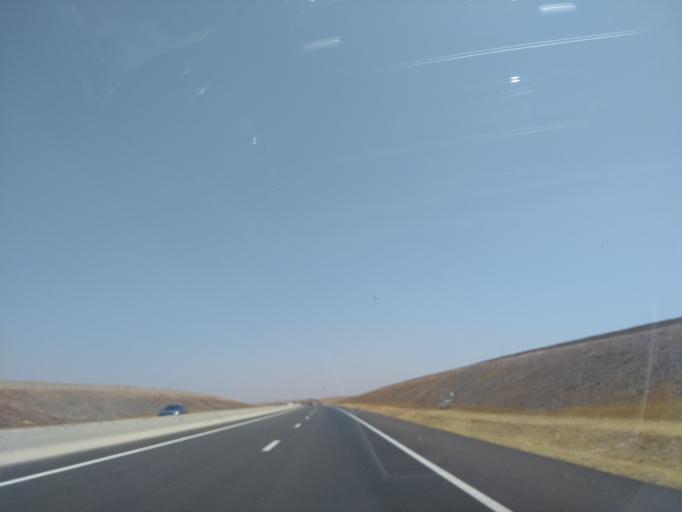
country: MA
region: Marrakech-Tensift-Al Haouz
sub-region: Kelaa-Des-Sraghna
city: Sidi Abdallah
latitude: 32.2927
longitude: -7.9621
